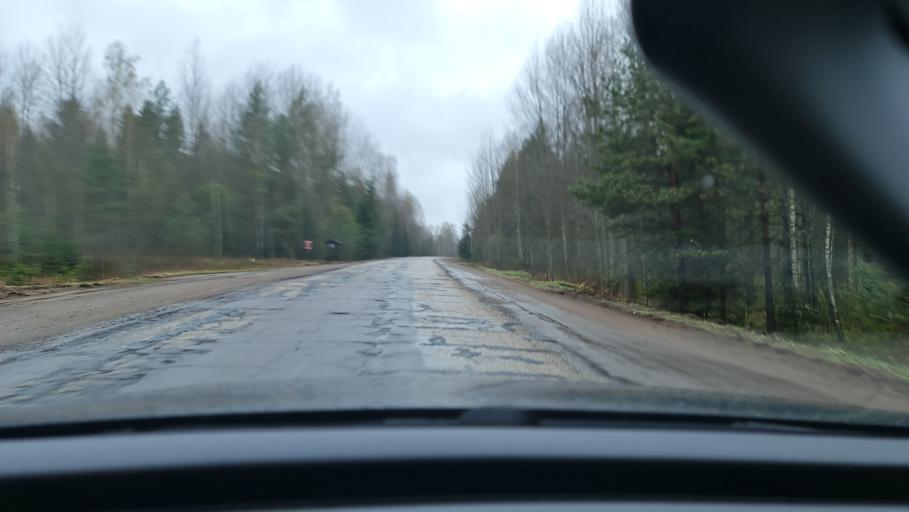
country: RU
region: Novgorod
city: Valday
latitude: 58.0370
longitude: 32.8940
